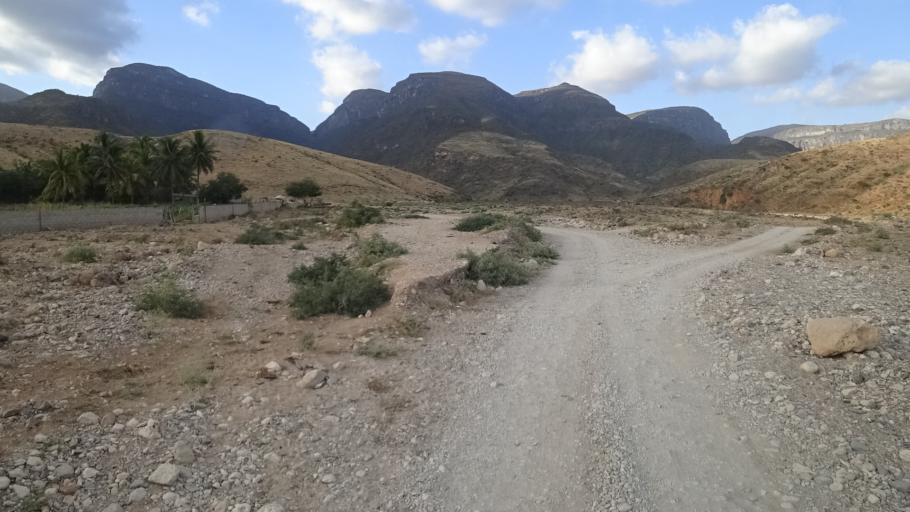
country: OM
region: Zufar
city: Salalah
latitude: 16.9912
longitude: 53.8468
